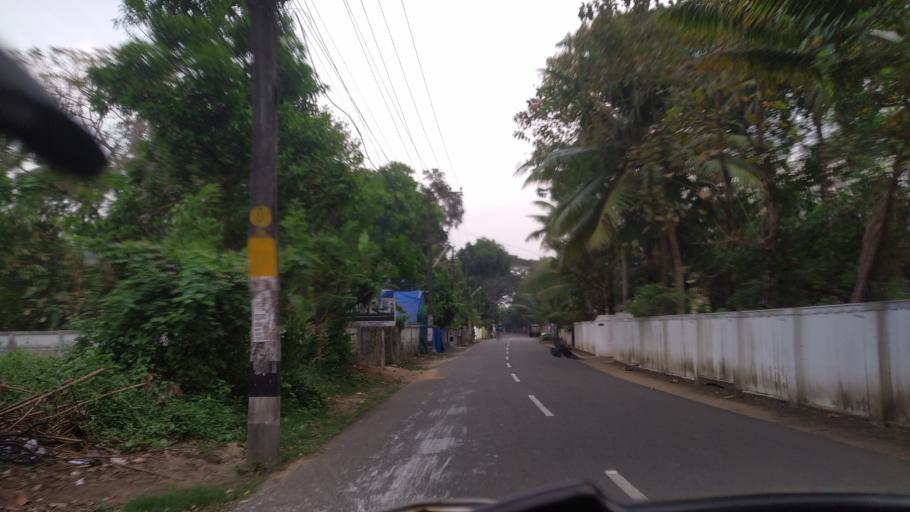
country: IN
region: Kerala
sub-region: Ernakulam
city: Elur
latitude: 10.1424
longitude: 76.2473
